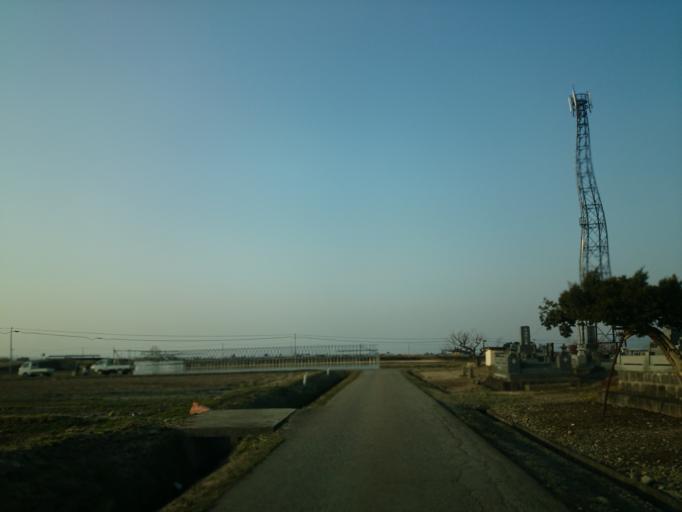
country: JP
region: Fukushima
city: Kitakata
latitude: 37.4430
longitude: 139.8587
